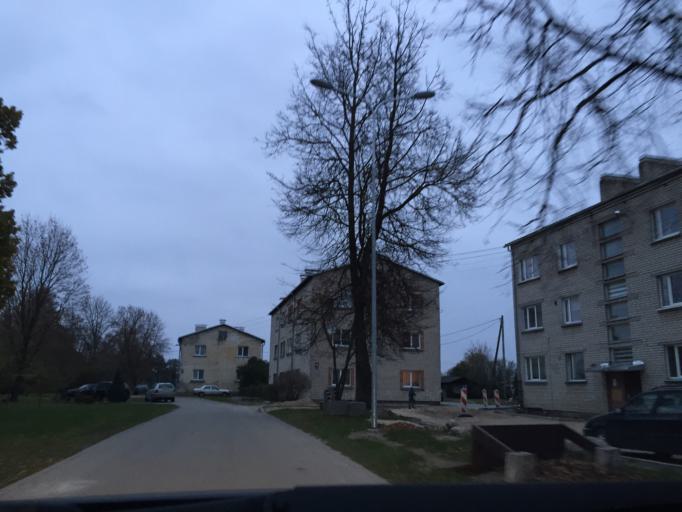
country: LV
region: Olaine
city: Olaine
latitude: 56.8017
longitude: 23.9858
